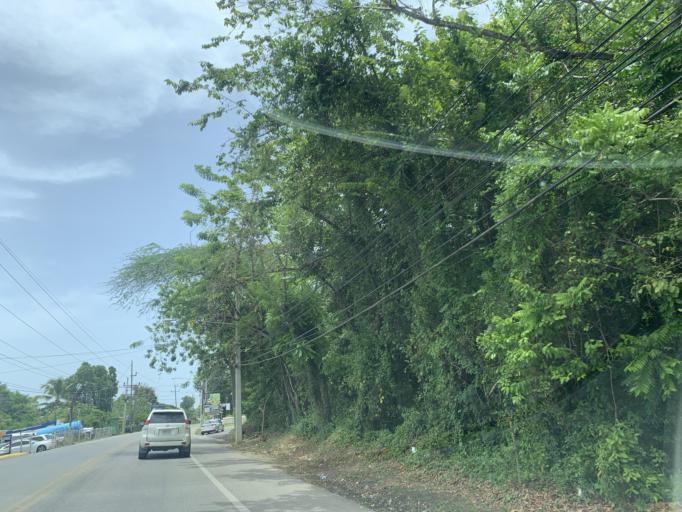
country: DO
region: Puerto Plata
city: Cabarete
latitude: 19.7693
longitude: -70.5043
